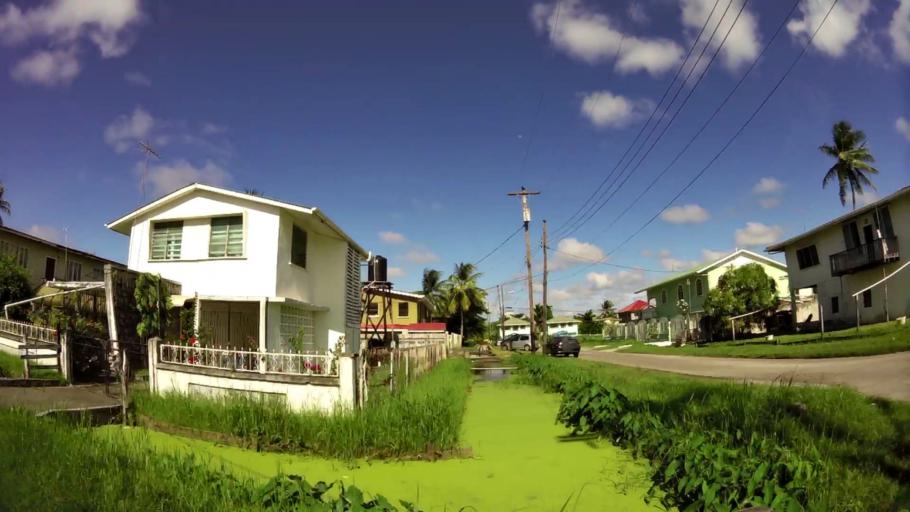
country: GY
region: Demerara-Mahaica
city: Georgetown
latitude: 6.8197
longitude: -58.1328
